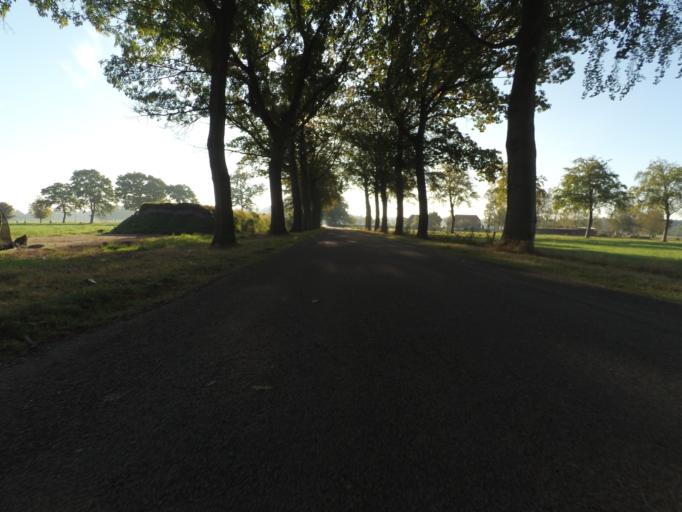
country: NL
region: Gelderland
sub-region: Gemeente Epe
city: Vaassen
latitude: 52.2954
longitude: 5.9524
